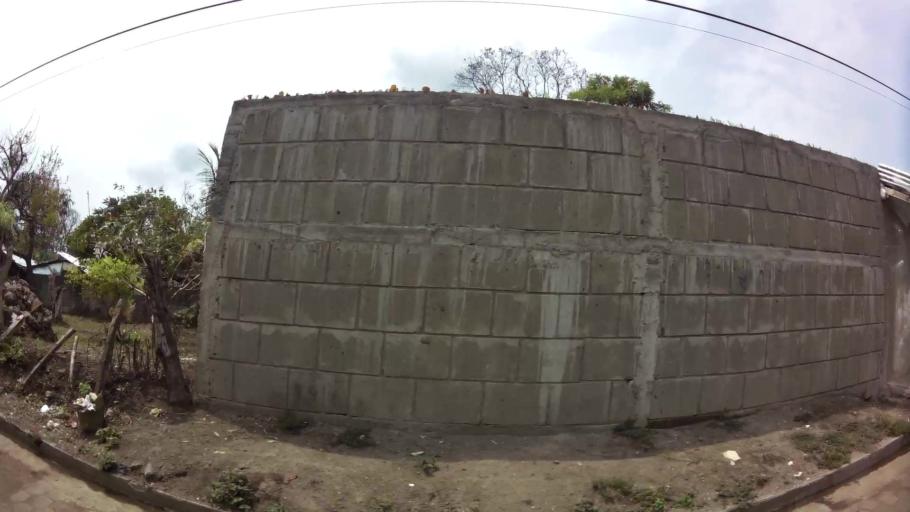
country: NI
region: Granada
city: Diriomo
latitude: 11.8746
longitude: -86.0491
